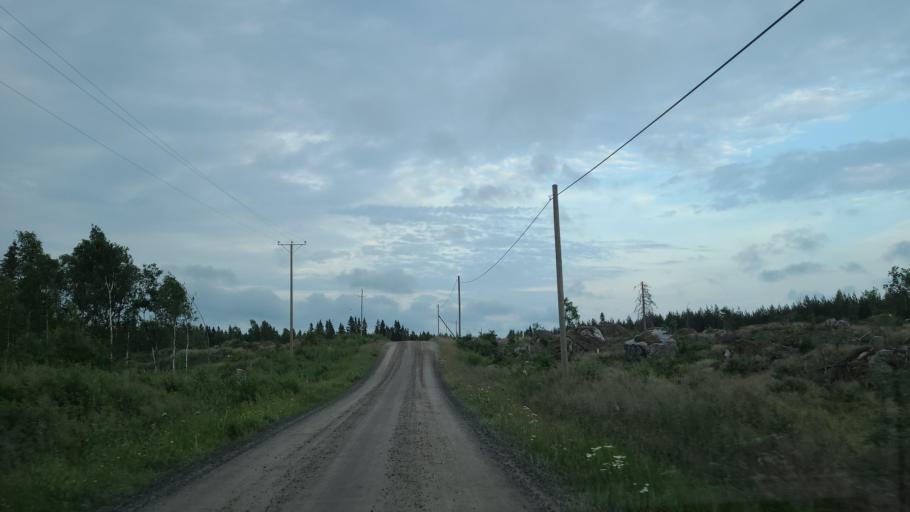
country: FI
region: Ostrobothnia
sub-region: Vaasa
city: Replot
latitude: 63.3184
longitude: 21.1494
